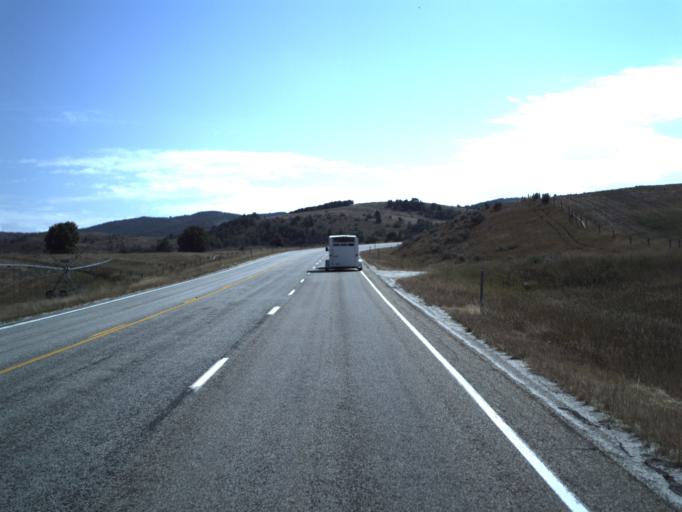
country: US
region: Utah
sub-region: Morgan County
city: Mountain Green
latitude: 41.2432
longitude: -111.7758
